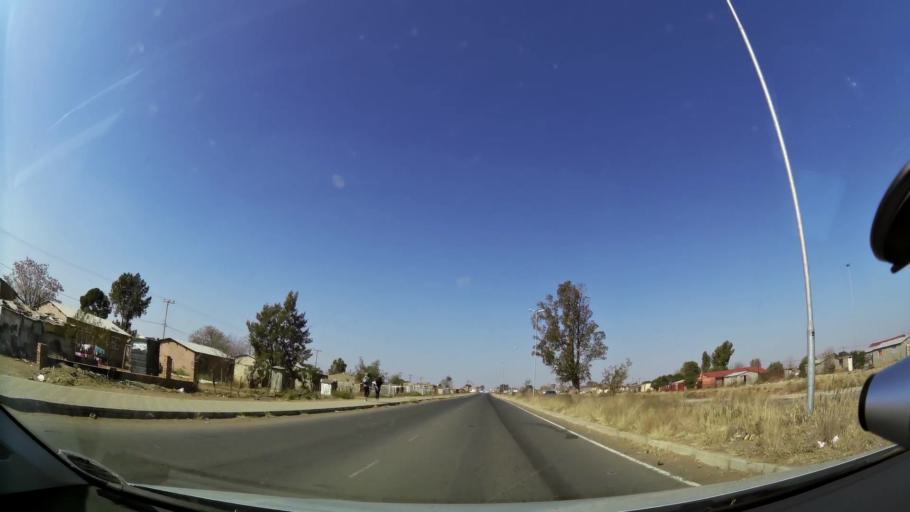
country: ZA
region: Orange Free State
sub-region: Mangaung Metropolitan Municipality
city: Bloemfontein
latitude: -29.1559
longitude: 26.2742
